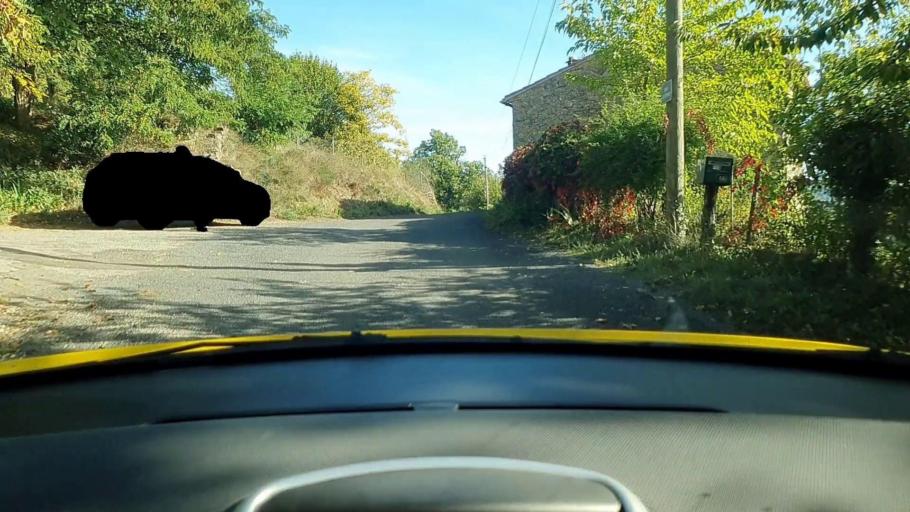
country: FR
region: Languedoc-Roussillon
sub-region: Departement du Gard
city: Le Vigan
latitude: 44.0183
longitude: 3.6230
